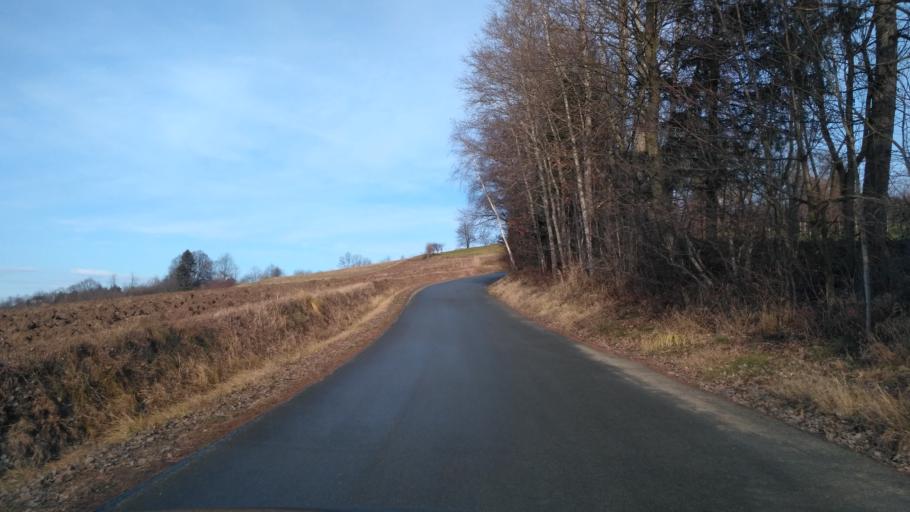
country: PL
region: Subcarpathian Voivodeship
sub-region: Powiat krosnienski
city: Korczyna
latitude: 49.7349
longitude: 21.7862
